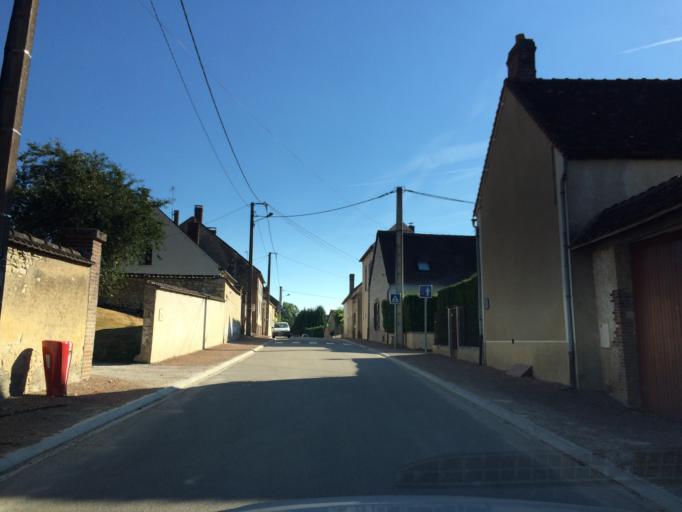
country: FR
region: Bourgogne
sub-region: Departement de l'Yonne
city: Fleury-la-Vallee
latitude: 47.8970
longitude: 3.4430
